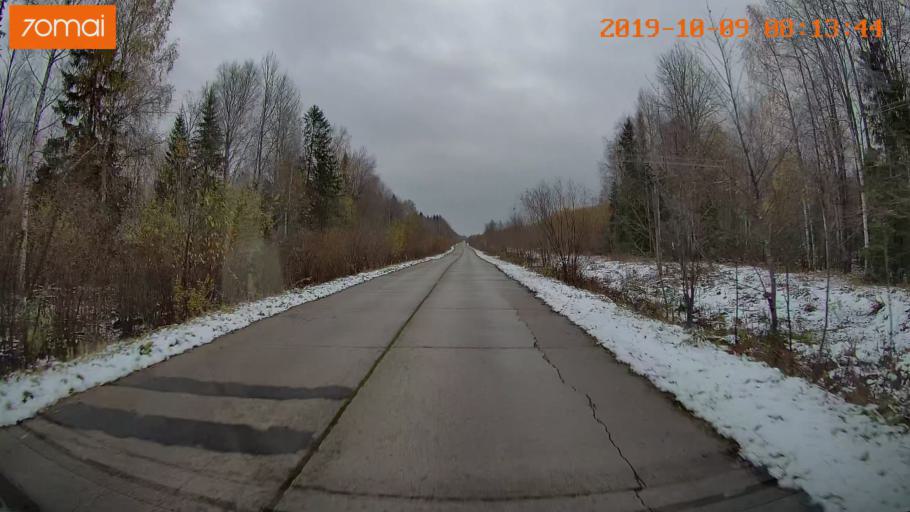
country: RU
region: Vologda
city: Gryazovets
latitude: 58.7249
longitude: 40.1444
